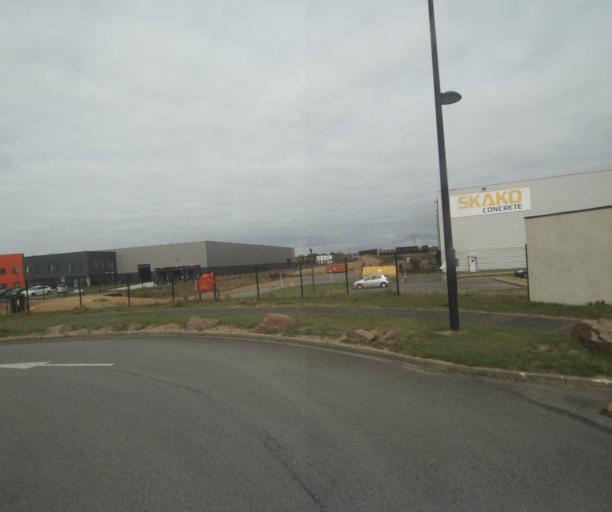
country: FR
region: Nord-Pas-de-Calais
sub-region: Departement du Nord
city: Lesquin
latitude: 50.5930
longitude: 3.1347
